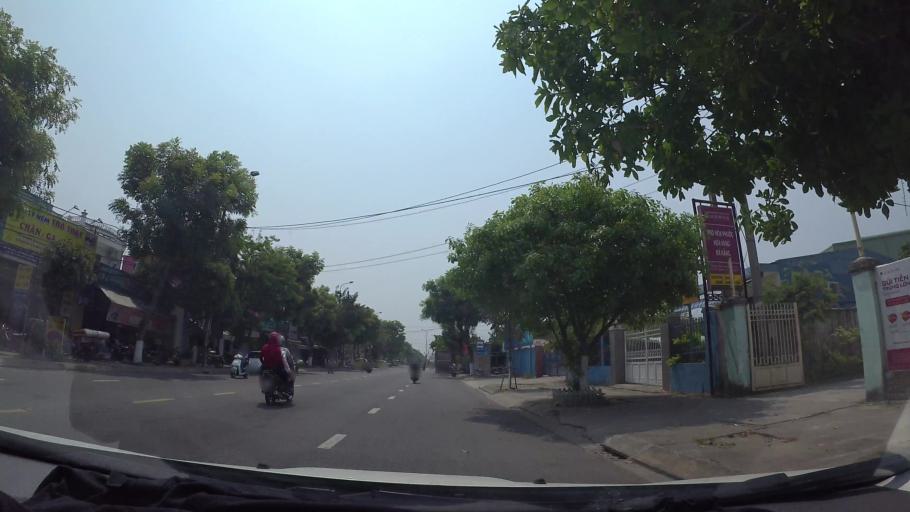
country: VN
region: Da Nang
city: Cam Le
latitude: 15.9819
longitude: 108.2081
